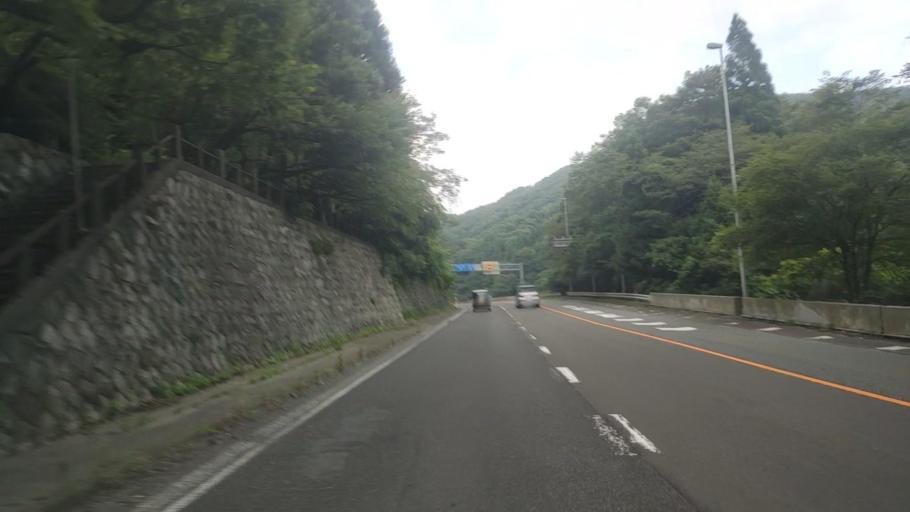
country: JP
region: Fukui
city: Takefu
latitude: 35.8347
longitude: 136.1198
